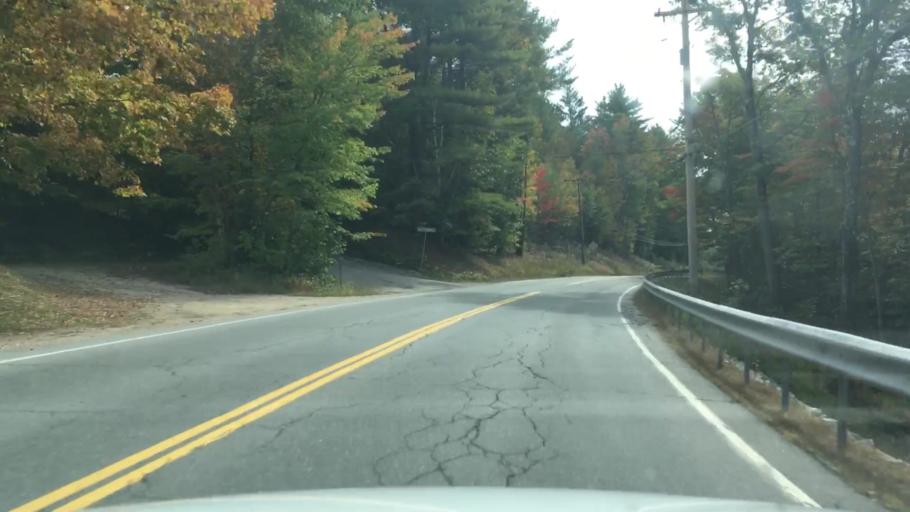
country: US
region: New Hampshire
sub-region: Carroll County
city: North Conway
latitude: 44.1532
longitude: -71.1977
